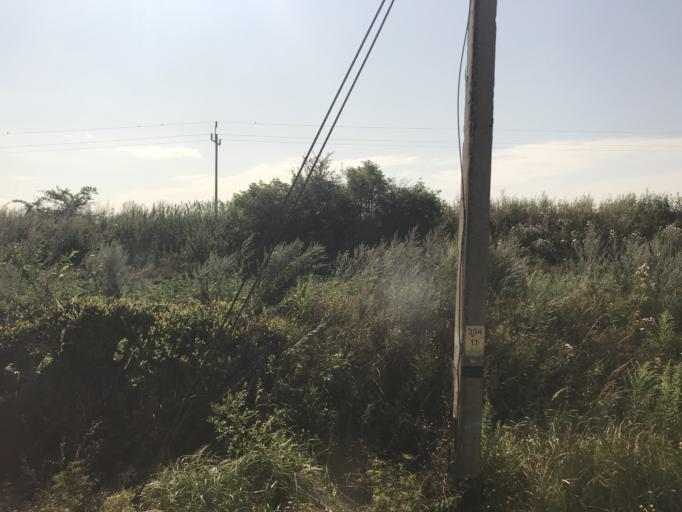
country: PL
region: Kujawsko-Pomorskie
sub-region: Powiat swiecki
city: Pruszcz
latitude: 53.3147
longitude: 18.1679
